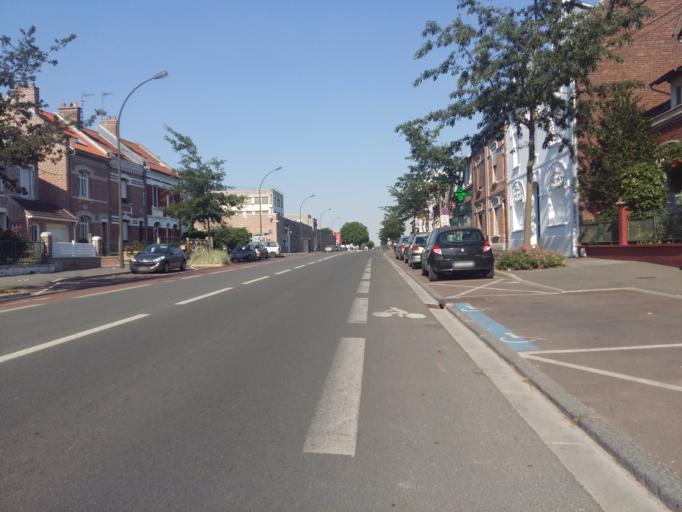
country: FR
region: Picardie
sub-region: Departement de la Somme
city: Rivery
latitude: 49.9079
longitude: 2.3223
